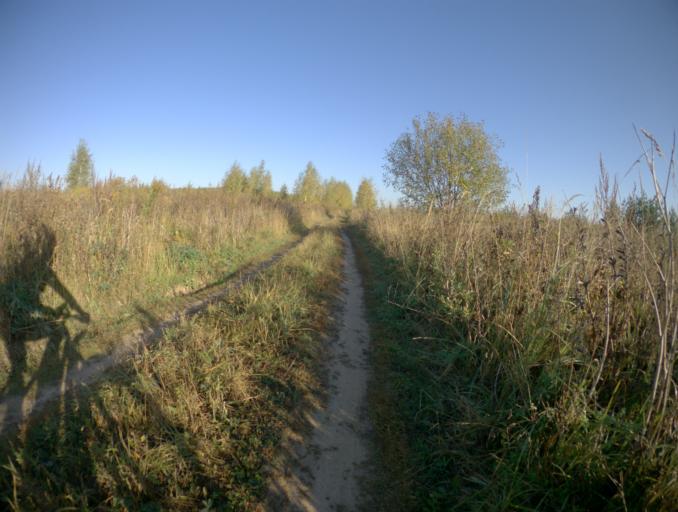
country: RU
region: Vladimir
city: Kideksha
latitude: 56.3567
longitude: 40.6721
